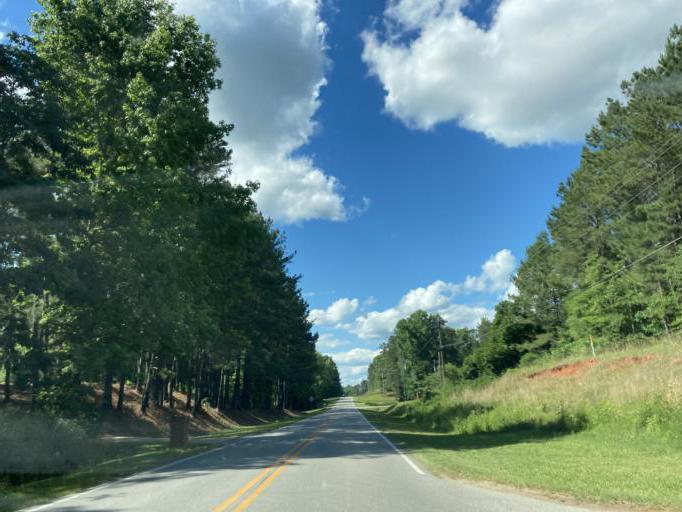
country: US
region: Georgia
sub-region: Jones County
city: Gray
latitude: 32.9862
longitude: -83.5504
